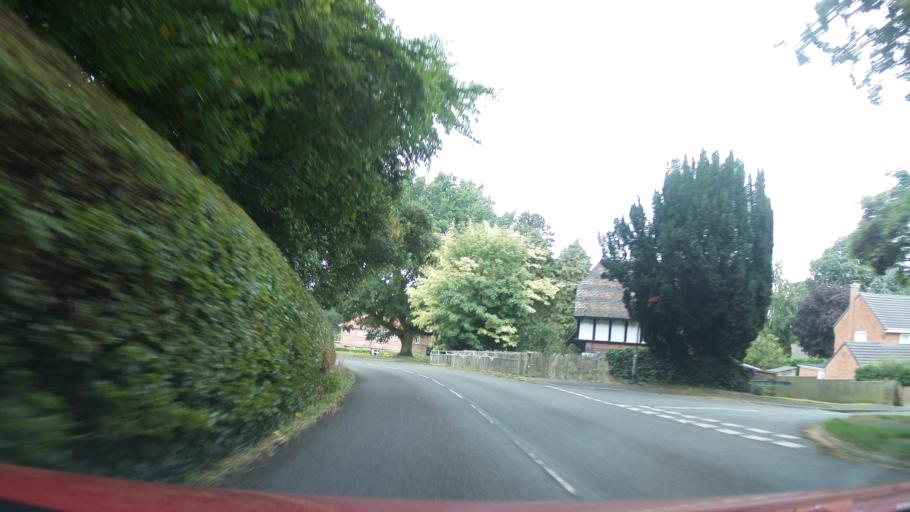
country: GB
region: England
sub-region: Staffordshire
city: Barlaston
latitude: 52.9164
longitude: -2.2237
